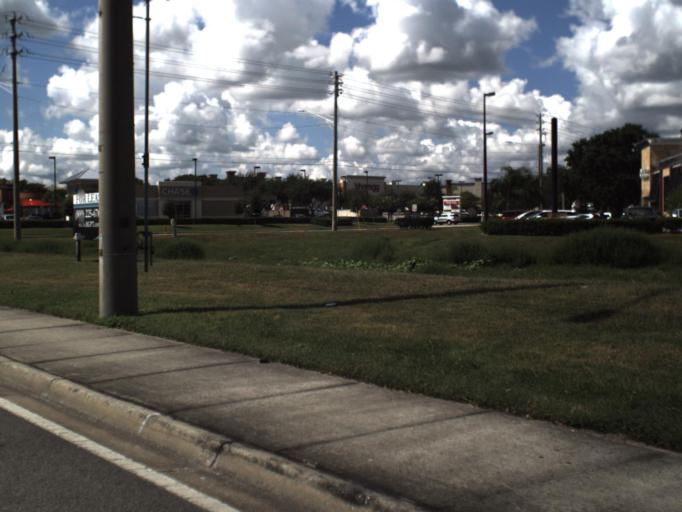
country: US
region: Florida
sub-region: Polk County
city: Gibsonia
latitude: 28.0962
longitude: -81.9739
